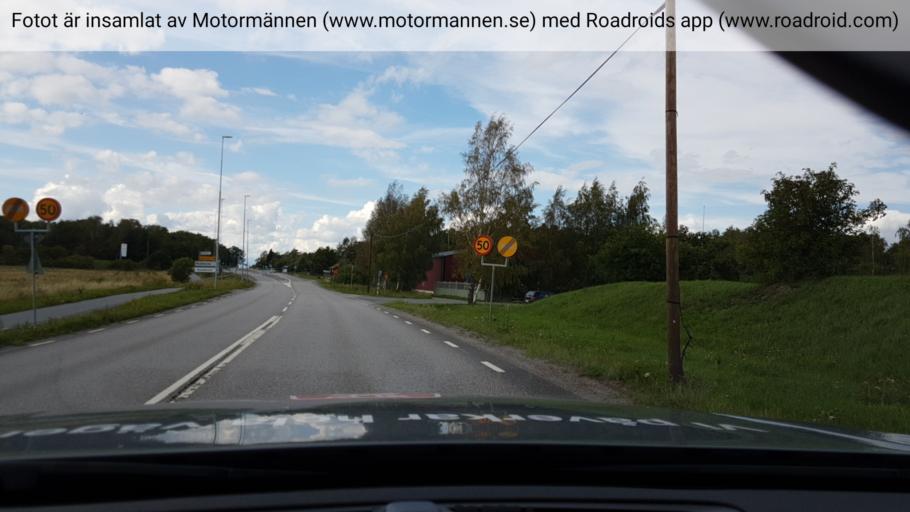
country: SE
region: Stockholm
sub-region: Upplands-Bro Kommun
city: Bro
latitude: 59.4930
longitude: 17.6852
